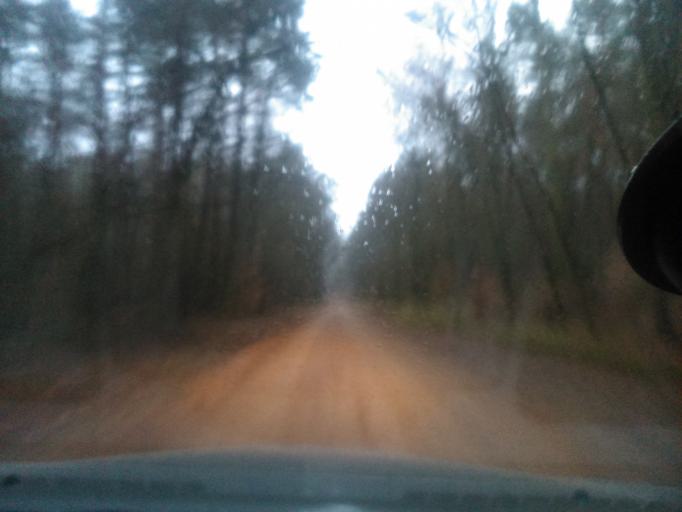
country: PL
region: Kujawsko-Pomorskie
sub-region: Powiat golubsko-dobrzynski
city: Radomin
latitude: 53.1539
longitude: 19.2034
